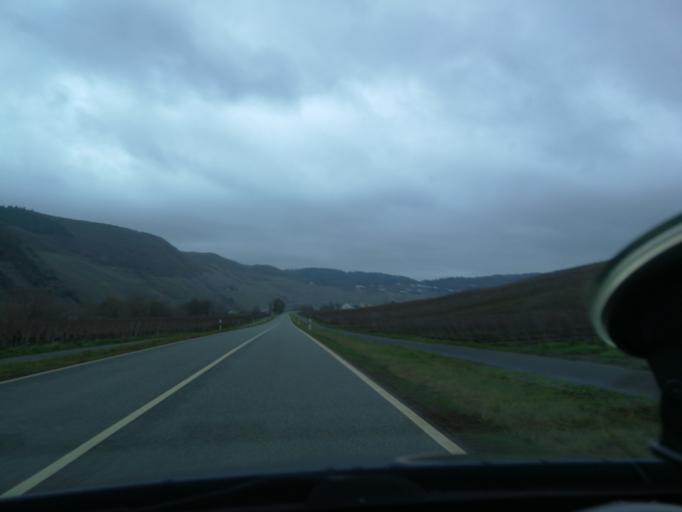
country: DE
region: Rheinland-Pfalz
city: Trittenheim
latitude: 49.8357
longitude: 6.8952
